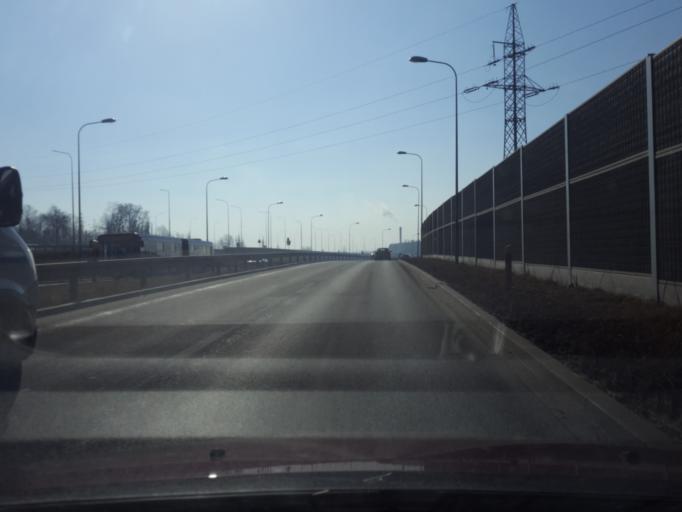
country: PL
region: Lesser Poland Voivodeship
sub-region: Powiat wielicki
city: Kokotow
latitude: 50.0673
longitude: 20.0683
